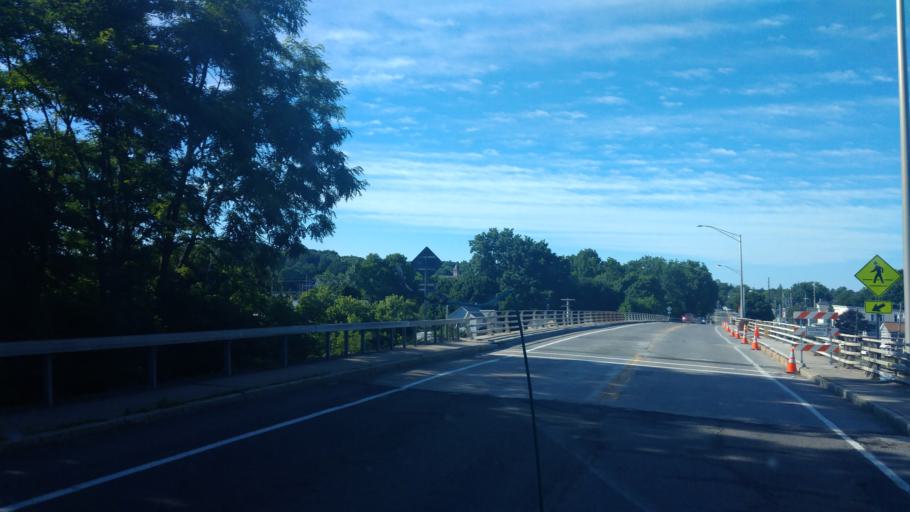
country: US
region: New York
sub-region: Wayne County
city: Lyons
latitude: 43.0568
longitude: -76.9933
